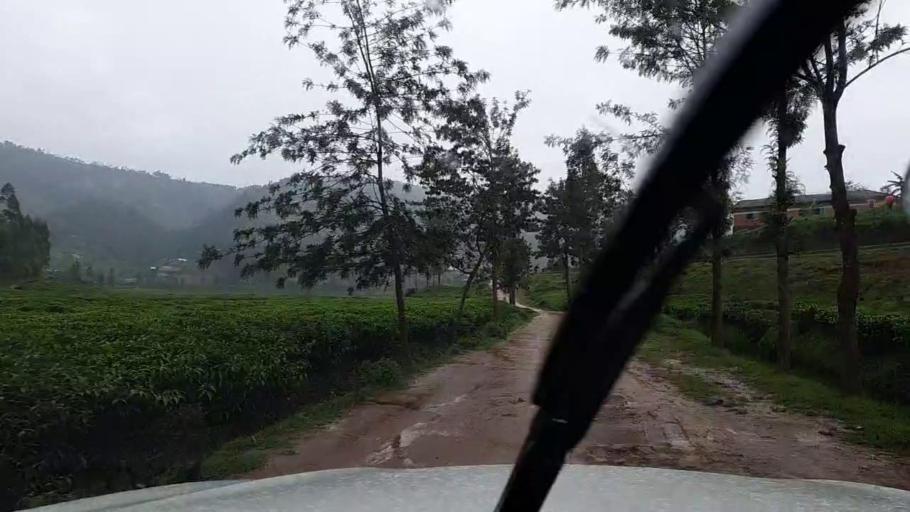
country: RW
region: Northern Province
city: Byumba
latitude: -1.6532
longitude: 29.9140
